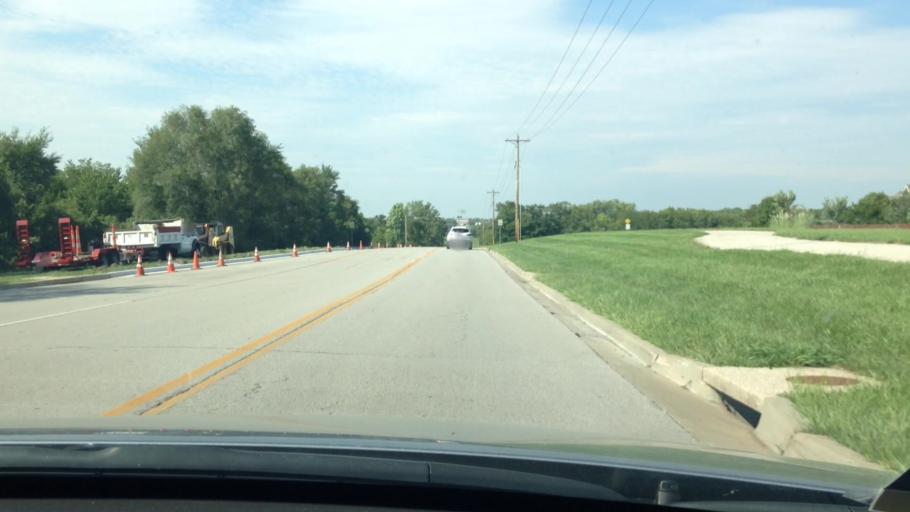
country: US
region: Missouri
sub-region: Platte County
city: Platte City
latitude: 39.3281
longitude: -94.7610
